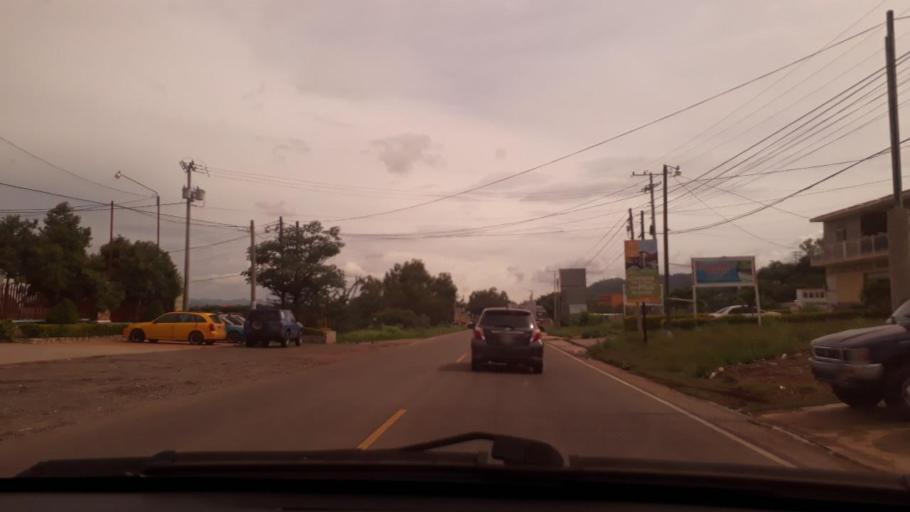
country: GT
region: Jutiapa
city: El Progreso
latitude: 14.3426
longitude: -89.8514
